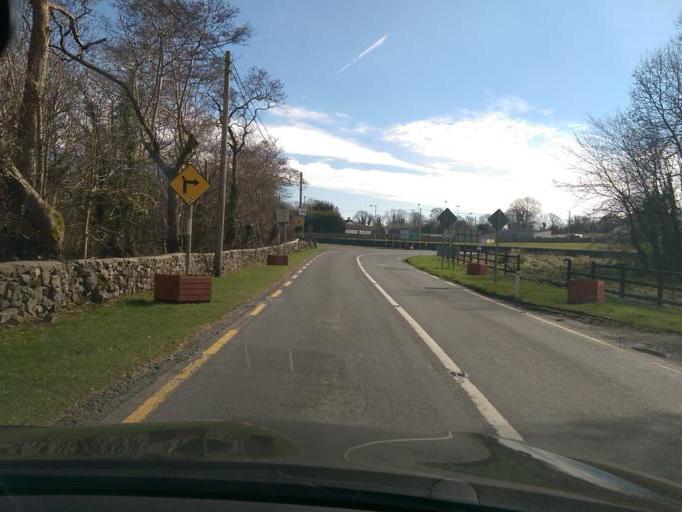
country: IE
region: Connaught
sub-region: County Galway
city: Tuam
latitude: 53.4405
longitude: -8.7275
